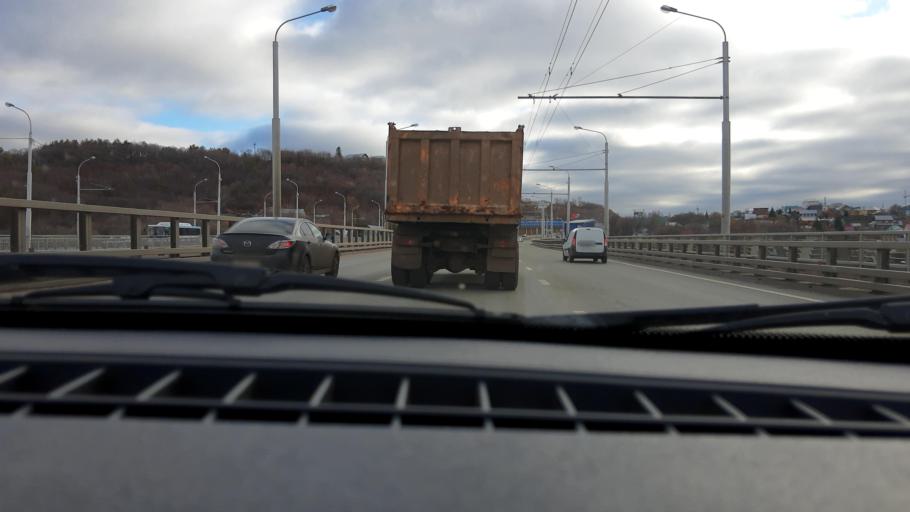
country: RU
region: Bashkortostan
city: Ufa
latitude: 54.7560
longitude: 55.9643
